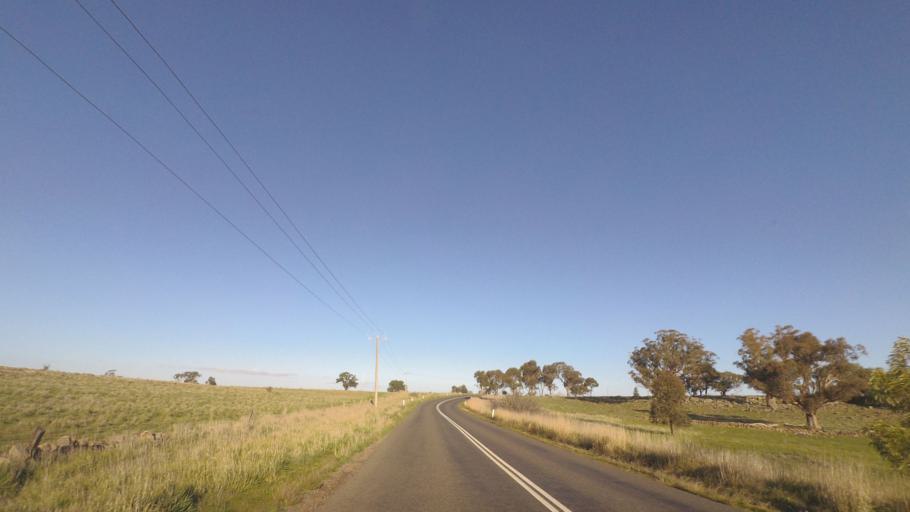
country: AU
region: Victoria
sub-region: Greater Bendigo
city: Kennington
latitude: -36.8191
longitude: 144.5154
